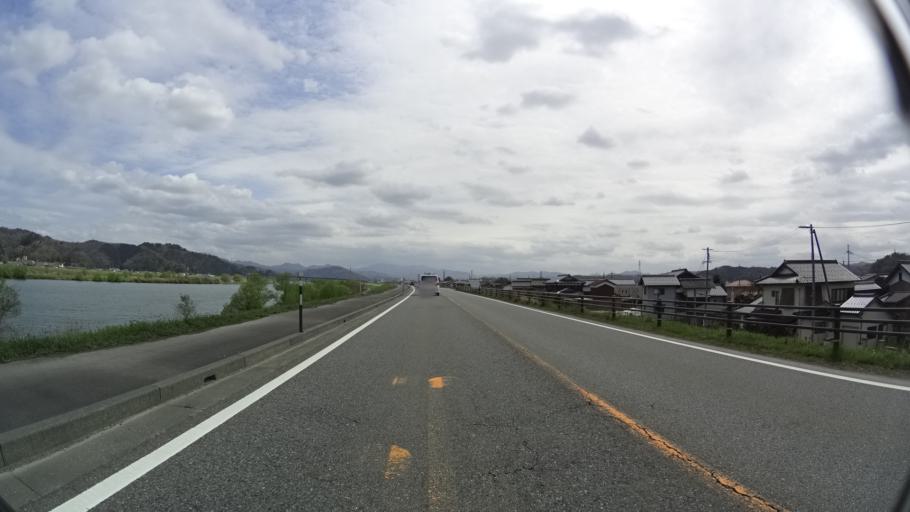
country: JP
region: Hyogo
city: Toyooka
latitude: 35.5640
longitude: 134.8123
